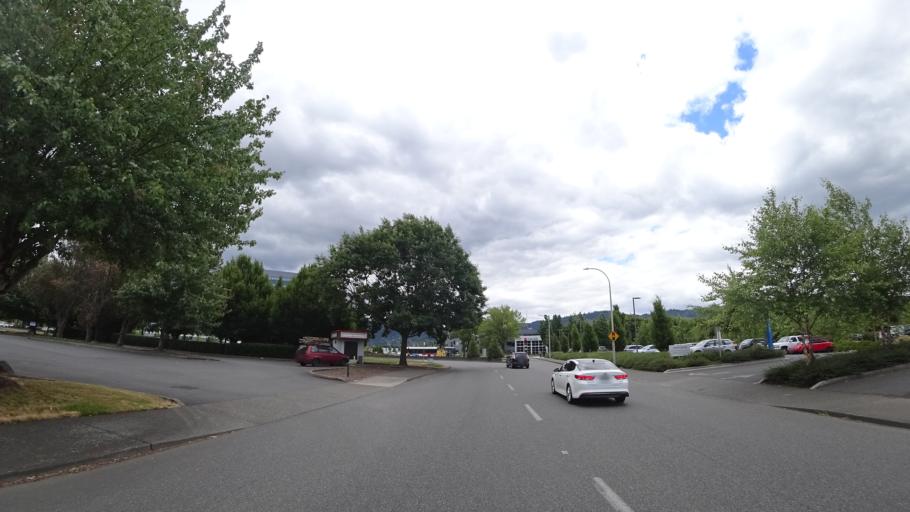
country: US
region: Oregon
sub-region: Multnomah County
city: Portland
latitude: 45.5575
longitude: -122.7034
